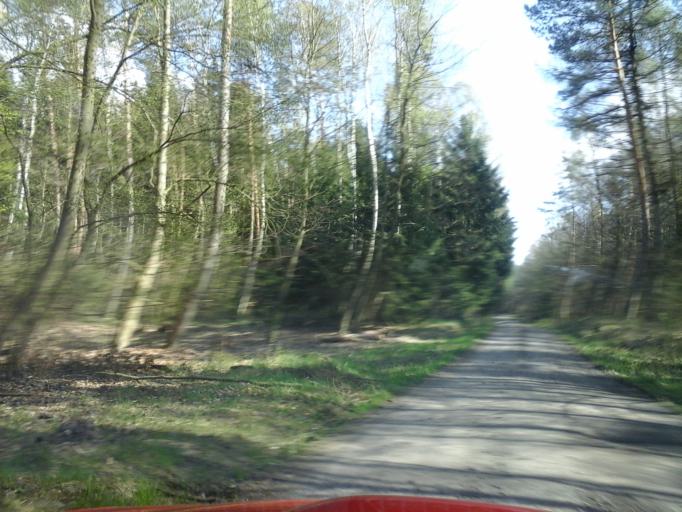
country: PL
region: West Pomeranian Voivodeship
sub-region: Powiat choszczenski
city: Bierzwnik
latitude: 53.0293
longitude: 15.6402
